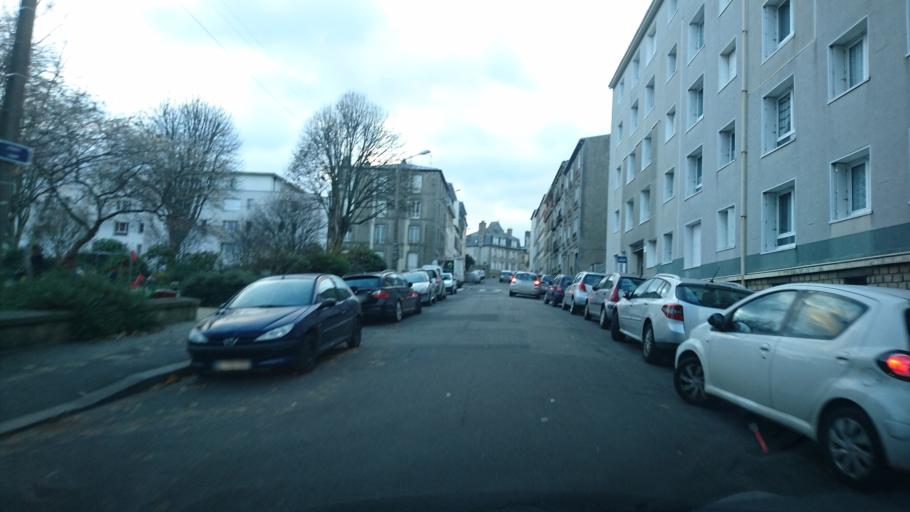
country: FR
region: Brittany
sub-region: Departement du Finistere
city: Brest
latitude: 48.3909
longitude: -4.4740
